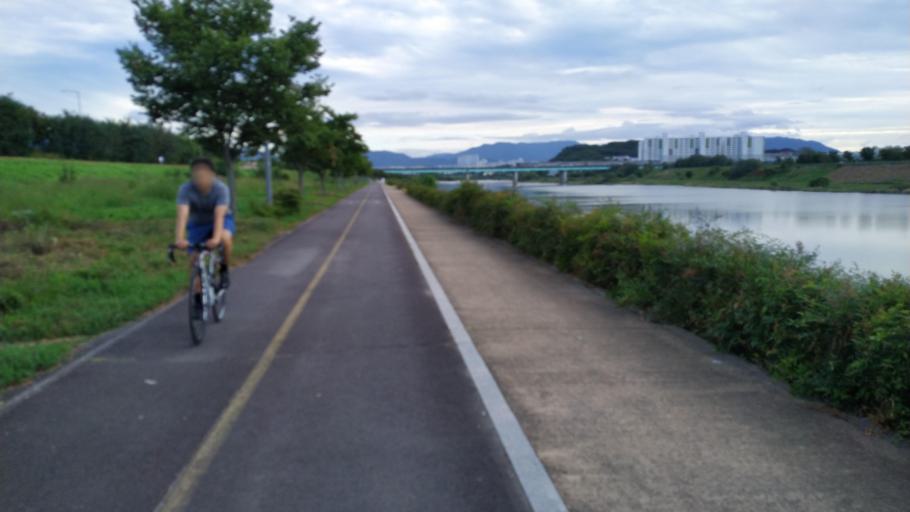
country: KR
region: Daegu
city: Daegu
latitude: 35.9237
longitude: 128.6326
